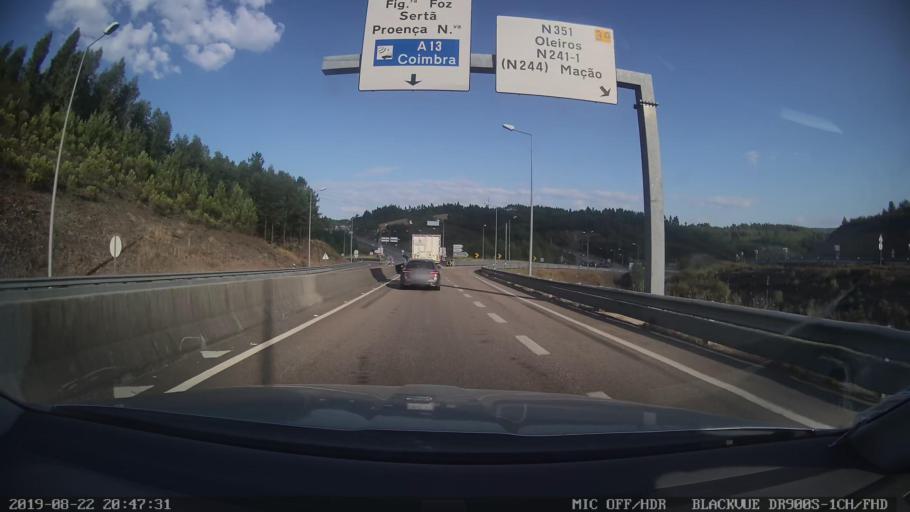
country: PT
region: Castelo Branco
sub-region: Proenca-A-Nova
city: Proenca-a-Nova
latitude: 39.7332
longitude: -7.8906
